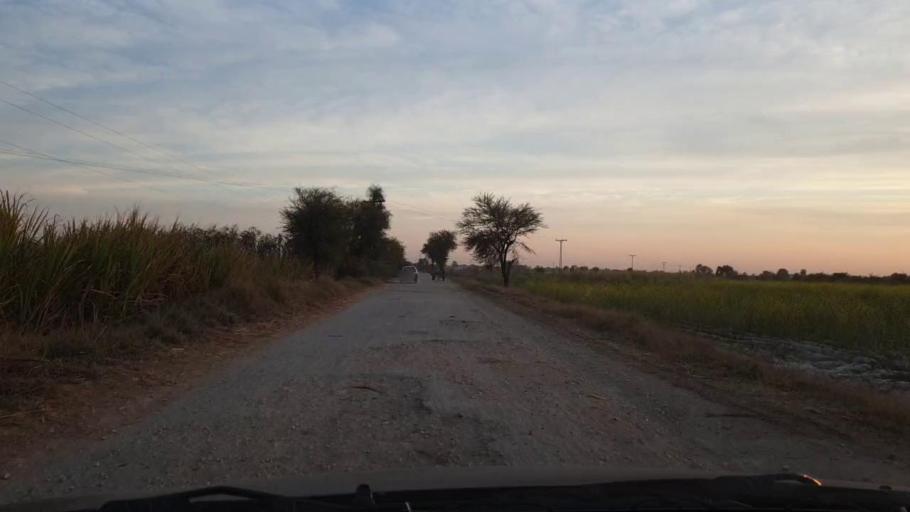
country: PK
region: Sindh
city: Sinjhoro
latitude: 26.1130
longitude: 68.7963
